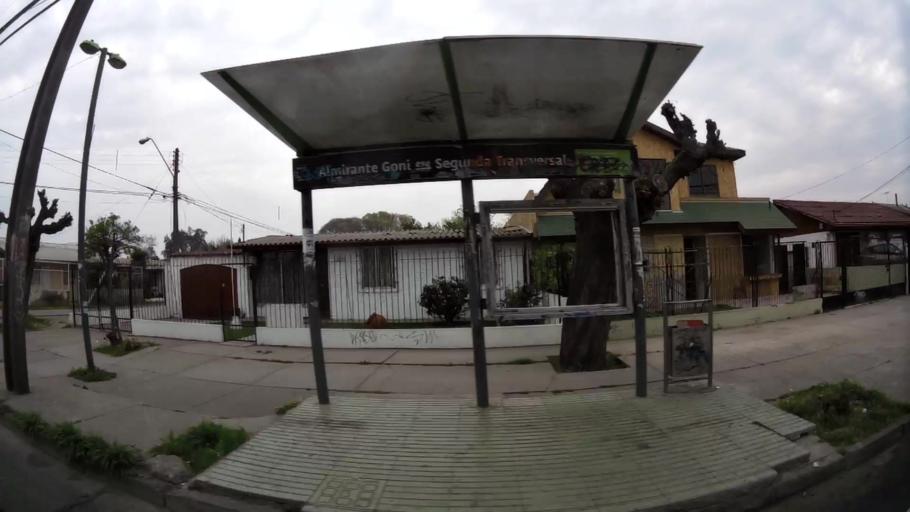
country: CL
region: Santiago Metropolitan
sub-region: Provincia de Santiago
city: Lo Prado
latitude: -33.5028
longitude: -70.7458
